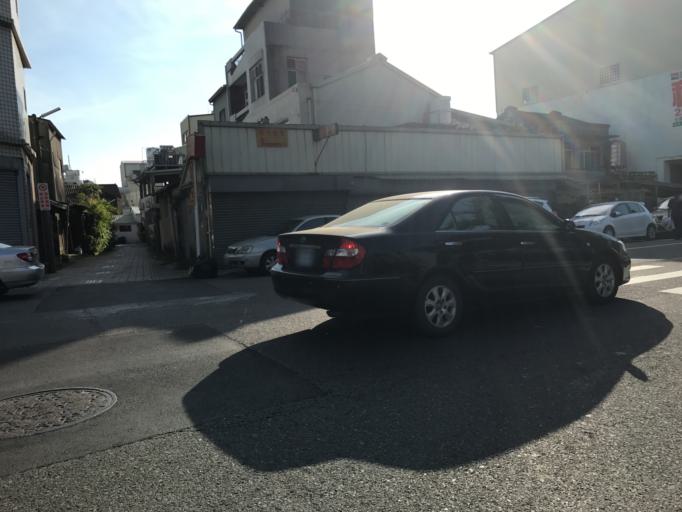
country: TW
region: Taiwan
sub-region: Tainan
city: Tainan
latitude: 23.0027
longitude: 120.1633
